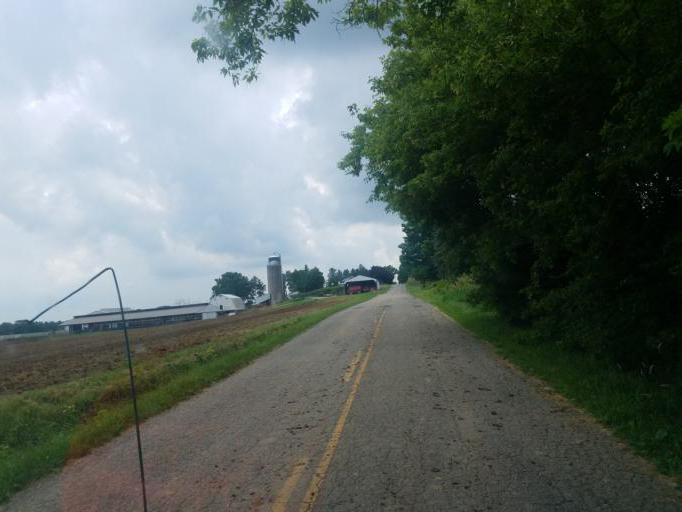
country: US
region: Ohio
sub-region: Columbiana County
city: Leetonia
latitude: 40.9237
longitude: -80.7410
